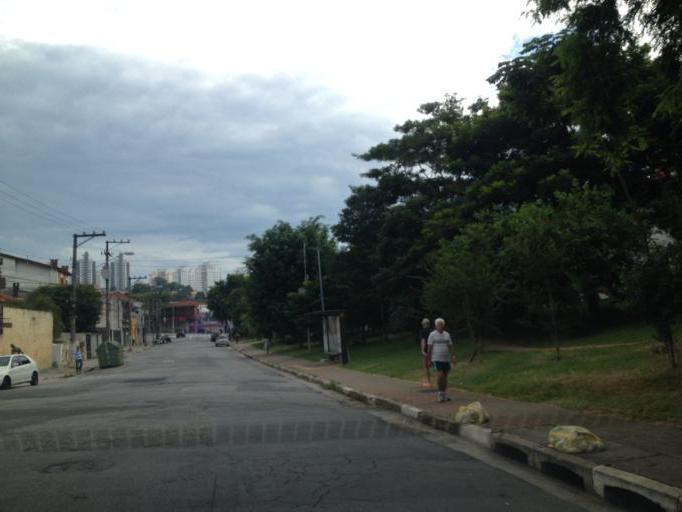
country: BR
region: Sao Paulo
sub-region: Osasco
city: Osasco
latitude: -23.5764
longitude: -46.7304
